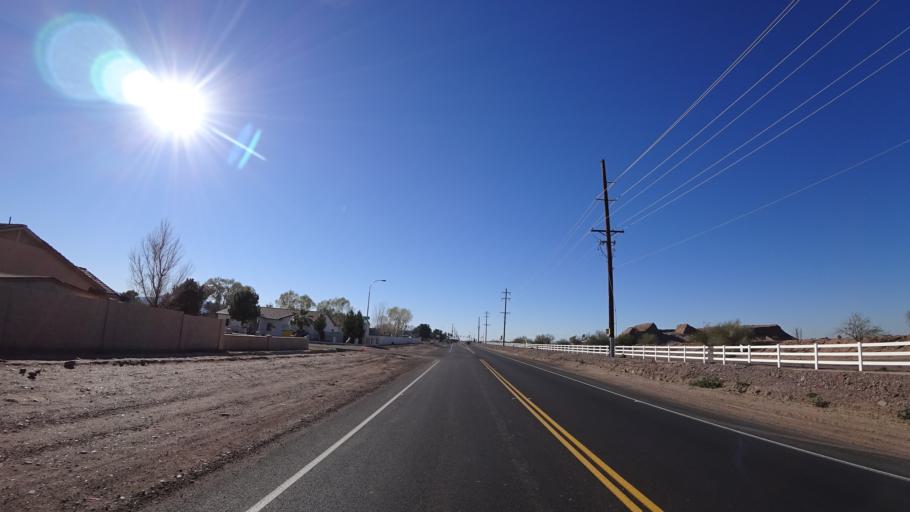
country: US
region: Arizona
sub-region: Maricopa County
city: Laveen
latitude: 33.3919
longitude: -112.1979
